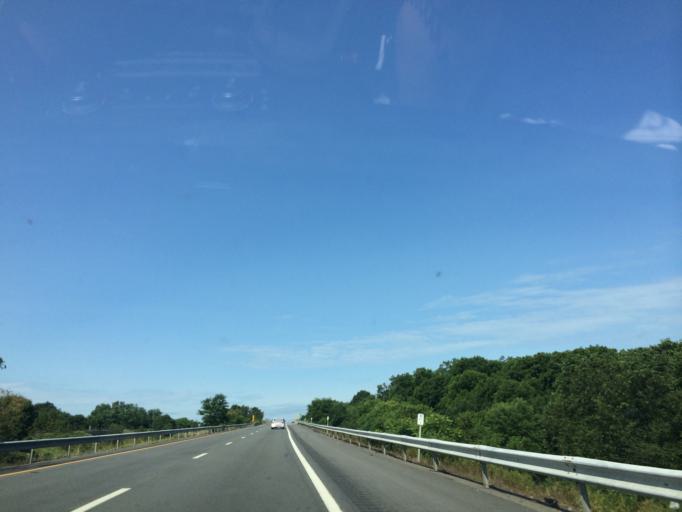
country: US
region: New York
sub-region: Orange County
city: Maybrook
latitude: 41.5013
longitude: -74.2362
